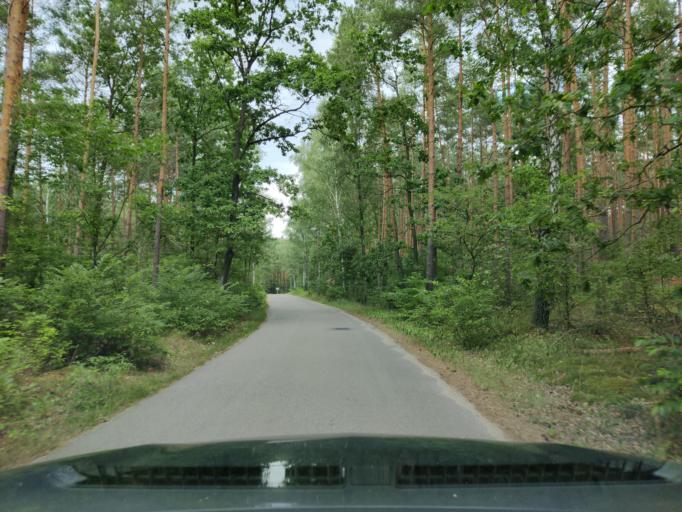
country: PL
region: Masovian Voivodeship
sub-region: Powiat pultuski
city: Pultusk
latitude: 52.7382
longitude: 21.1392
